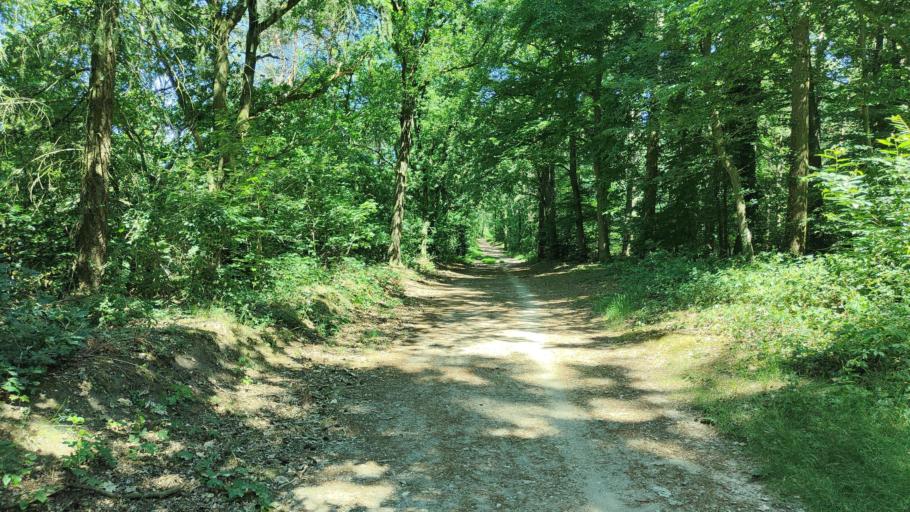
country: NL
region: North Brabant
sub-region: Gemeente Cuijk
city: Cuijk
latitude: 51.7712
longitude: 5.8818
